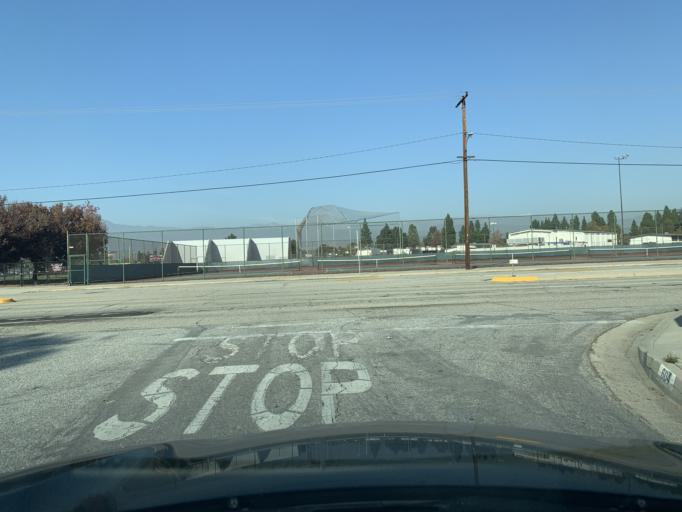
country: US
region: California
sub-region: Los Angeles County
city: Covina
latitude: 34.0789
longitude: -117.9018
